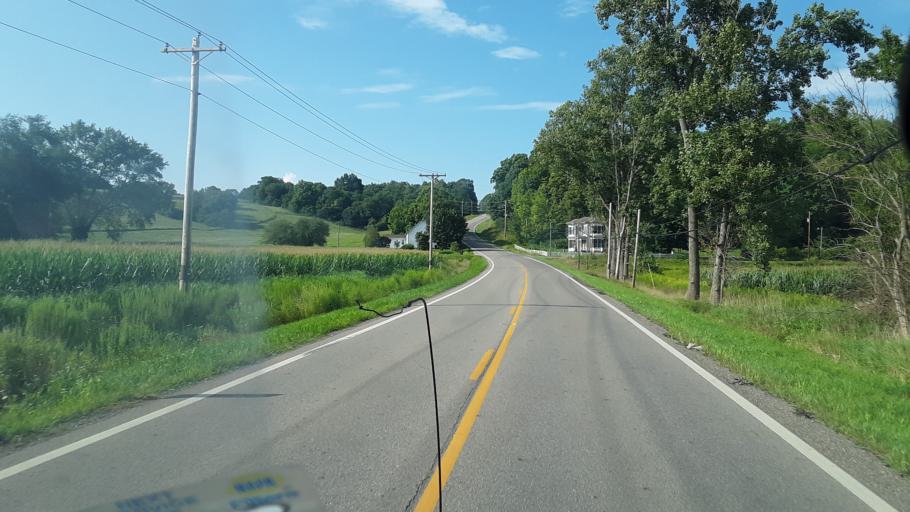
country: US
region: Ohio
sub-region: Licking County
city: Granville
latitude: 40.1248
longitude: -82.5175
